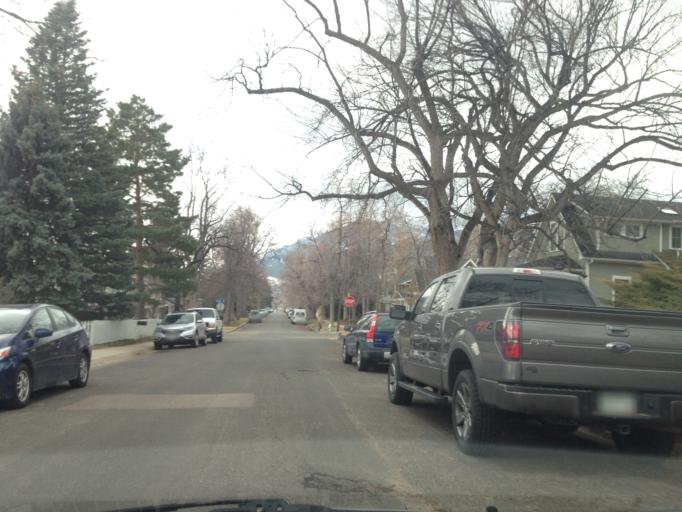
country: US
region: Colorado
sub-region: Boulder County
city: Boulder
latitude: 40.0334
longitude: -105.2904
